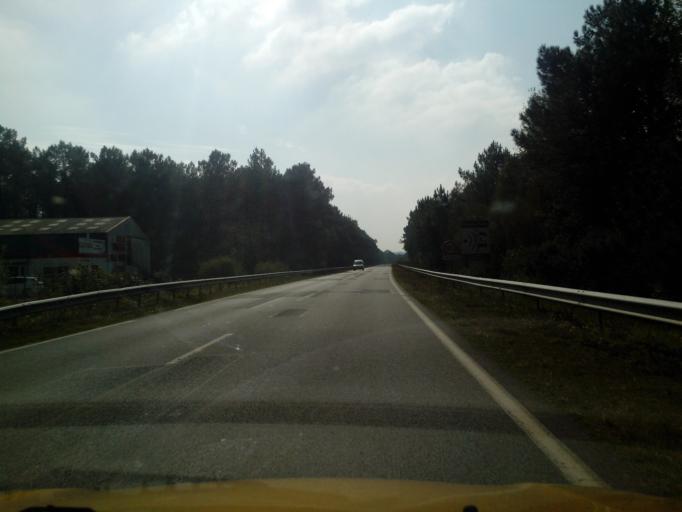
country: FR
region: Brittany
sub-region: Departement du Morbihan
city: Molac
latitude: 47.7432
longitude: -2.4374
